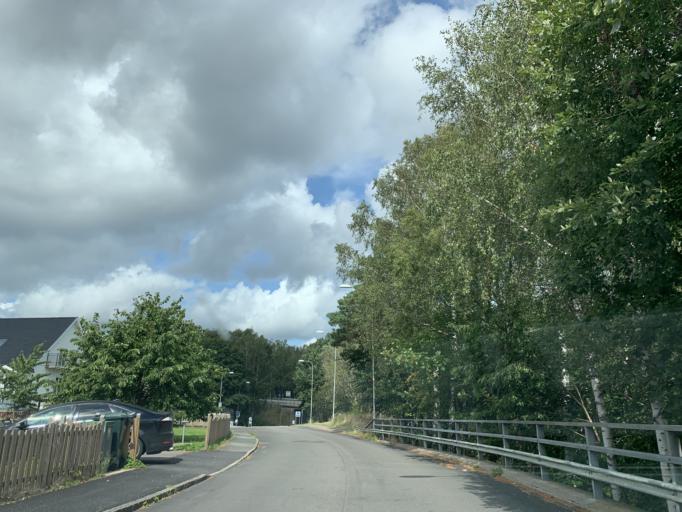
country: SE
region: Vaestra Goetaland
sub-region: Goteborg
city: Eriksbo
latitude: 57.7528
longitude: 12.0555
